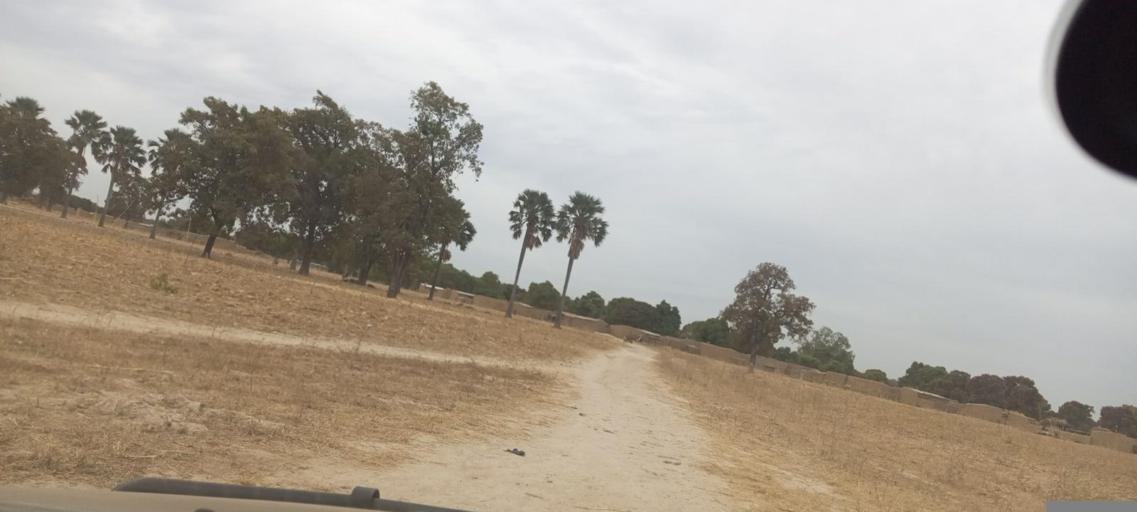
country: ML
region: Koulikoro
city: Kati
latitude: 12.7407
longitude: -8.3279
